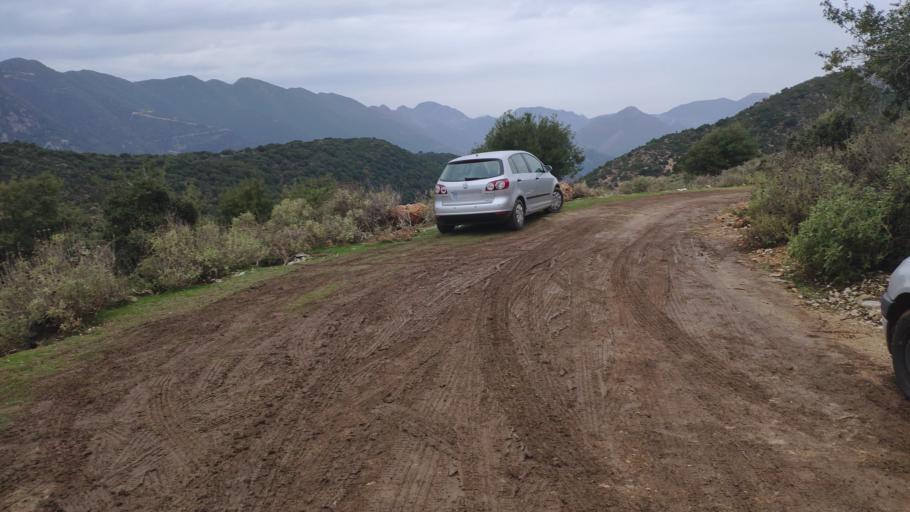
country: GR
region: Epirus
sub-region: Nomos Prevezis
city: Kanalaki
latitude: 39.3619
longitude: 20.6441
